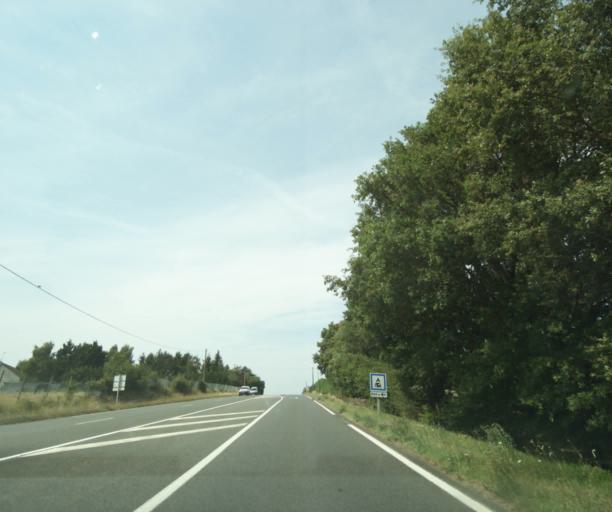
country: FR
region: Centre
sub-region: Departement d'Indre-et-Loire
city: Sainte-Maure-de-Touraine
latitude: 47.1506
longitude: 0.6466
